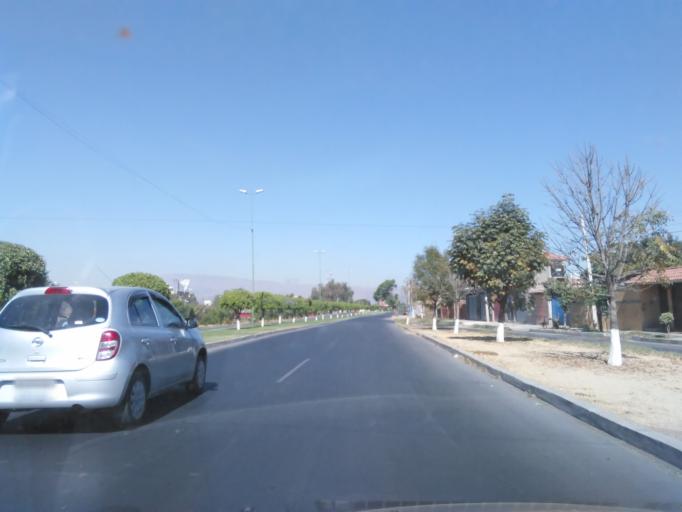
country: BO
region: Cochabamba
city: Cochabamba
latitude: -17.4042
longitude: -66.1704
